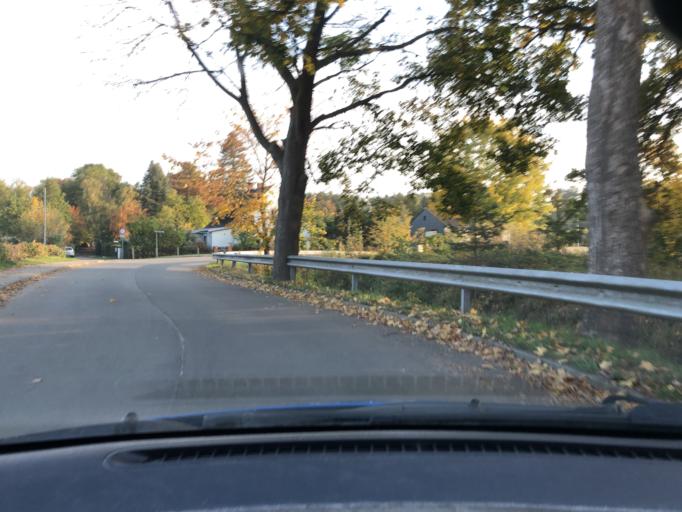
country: DE
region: Lower Saxony
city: Hitzacker
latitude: 53.1402
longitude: 11.0362
